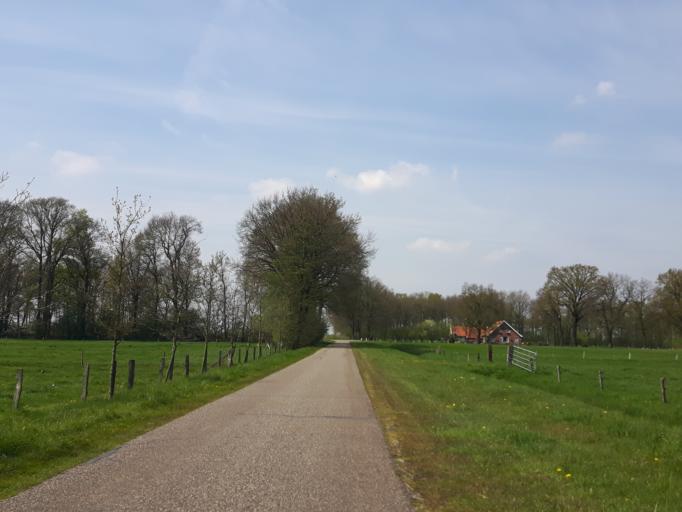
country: NL
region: Overijssel
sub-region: Gemeente Haaksbergen
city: Haaksbergen
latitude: 52.1233
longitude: 6.7972
